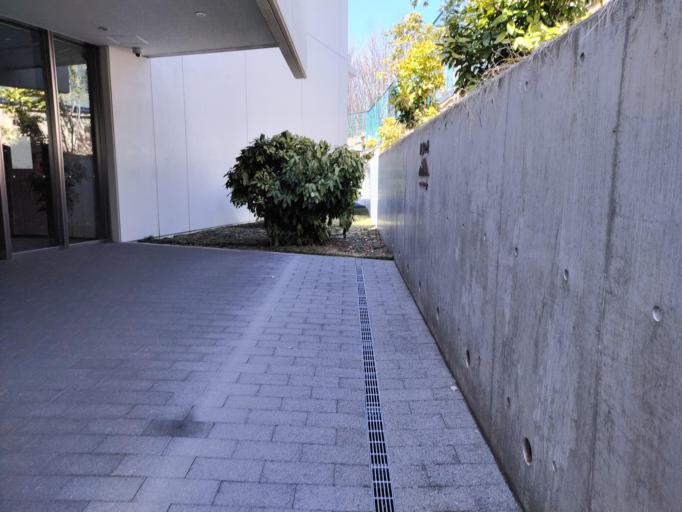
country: JP
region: Nagano
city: Komoro
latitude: 36.2935
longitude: 138.4753
